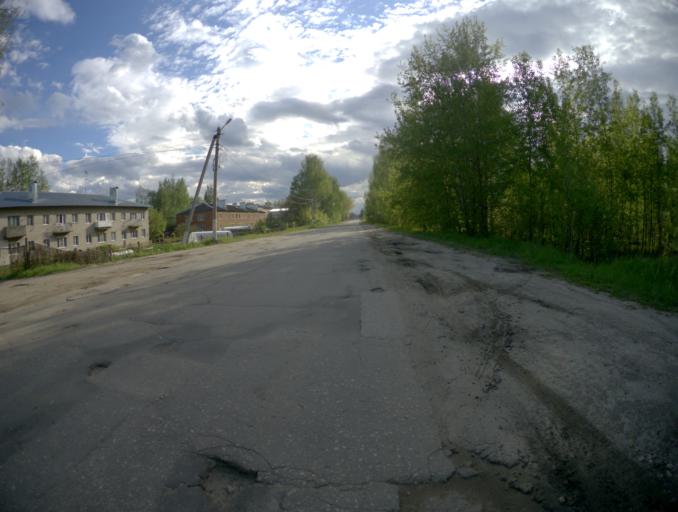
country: RU
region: Rjazan
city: Spas-Klepiki
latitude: 55.1396
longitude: 40.1968
